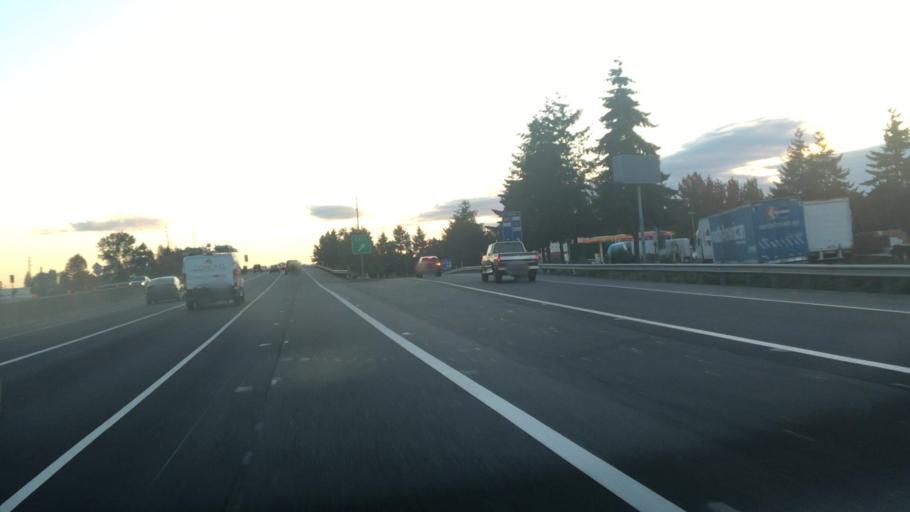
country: US
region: Washington
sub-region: King County
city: Kent
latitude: 47.4006
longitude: -122.2253
